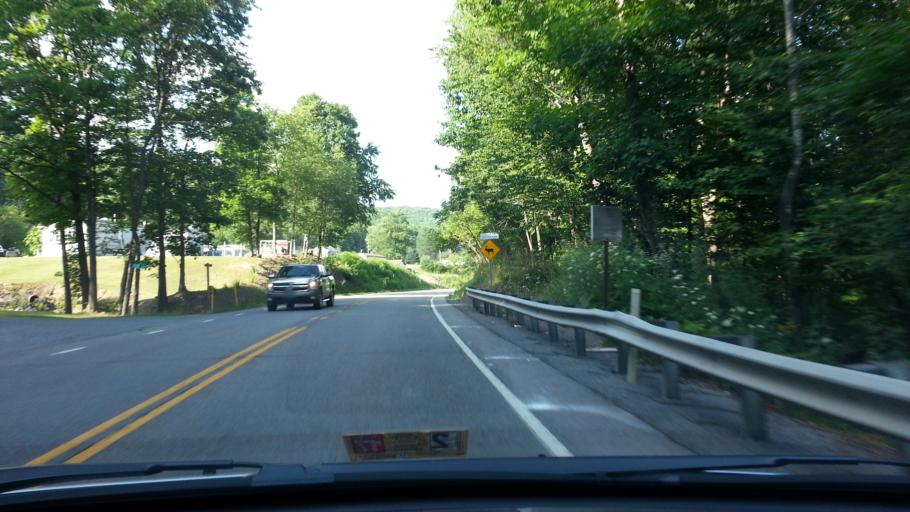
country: US
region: Pennsylvania
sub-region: Elk County
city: Saint Marys
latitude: 41.2461
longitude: -78.5279
